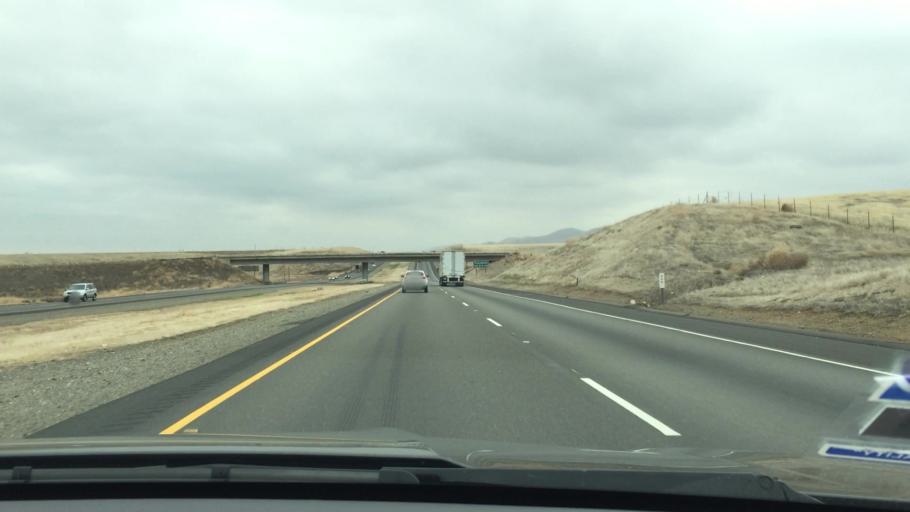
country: US
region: California
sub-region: Stanislaus County
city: Newman
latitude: 37.2621
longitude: -121.0931
